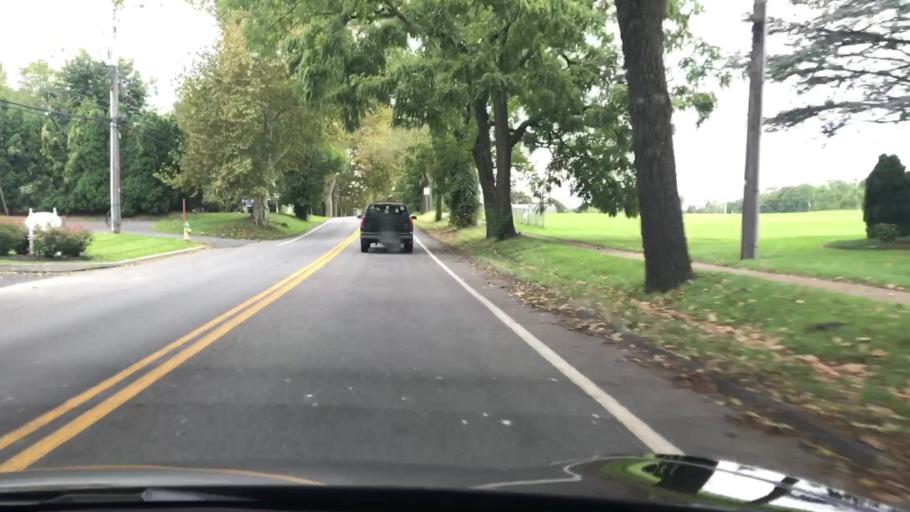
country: US
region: Pennsylvania
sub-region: Cumberland County
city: Shiremanstown
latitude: 40.2235
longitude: -76.9391
